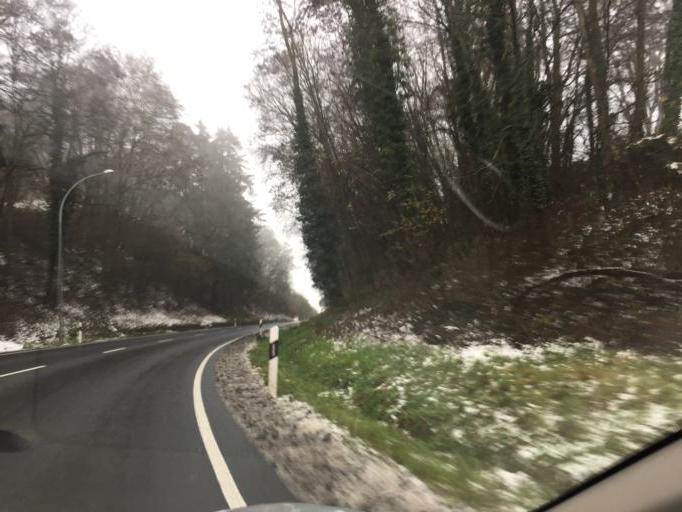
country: LU
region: Diekirch
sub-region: Canton de Diekirch
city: Niederfeulen
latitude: 49.8502
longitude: 6.0636
